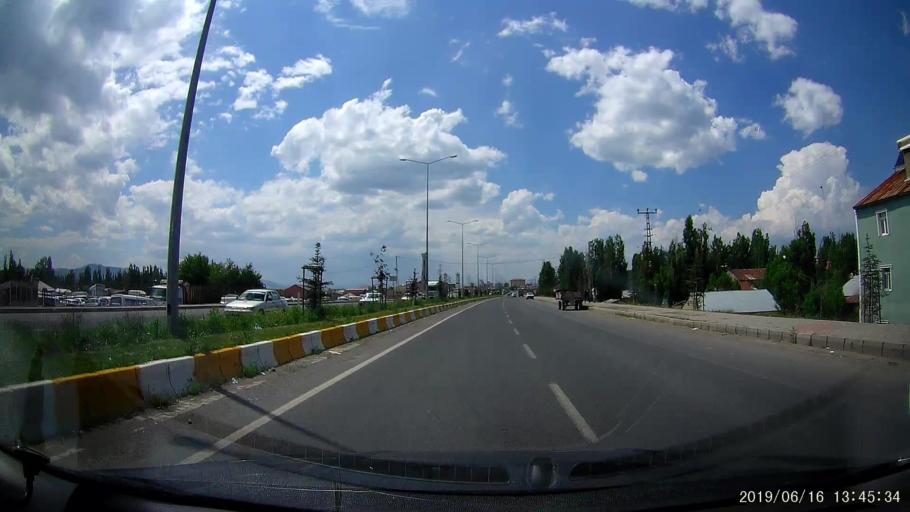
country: TR
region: Agri
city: Agri
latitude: 39.7093
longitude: 43.0440
